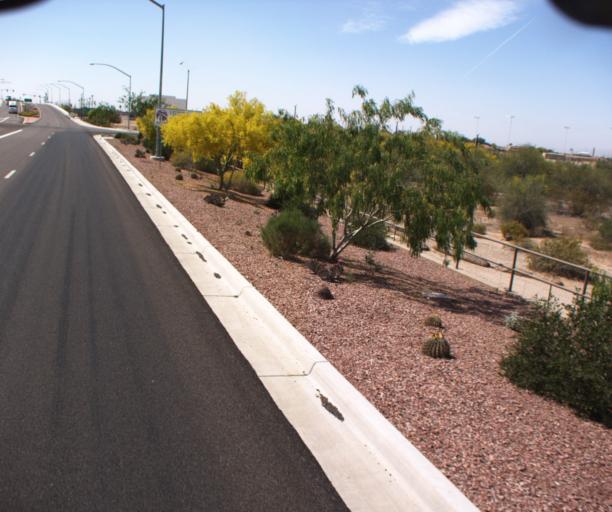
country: US
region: Arizona
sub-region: Maricopa County
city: Gila Bend
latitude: 32.9527
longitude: -112.6931
